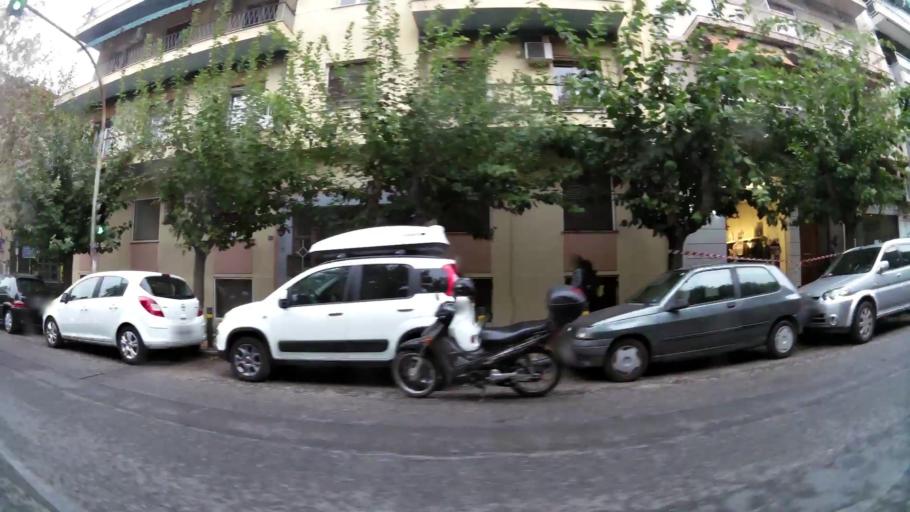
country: GR
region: Attica
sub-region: Nomarchia Athinas
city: Vyronas
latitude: 37.9686
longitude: 23.7472
